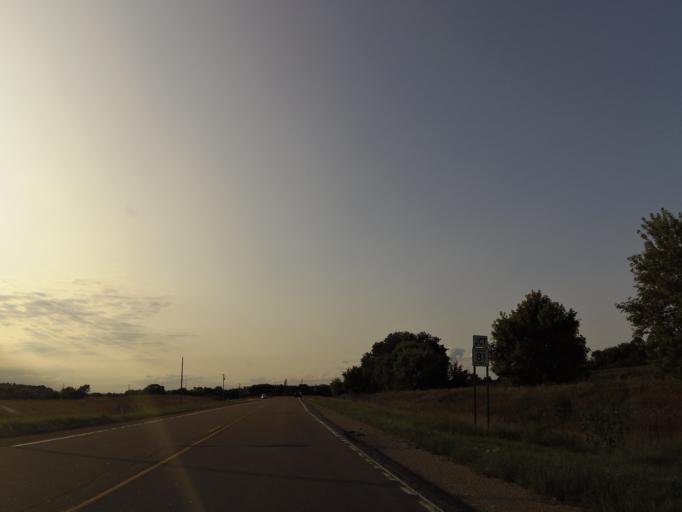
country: US
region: Minnesota
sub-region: Dakota County
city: Farmington
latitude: 44.6277
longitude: -93.0196
